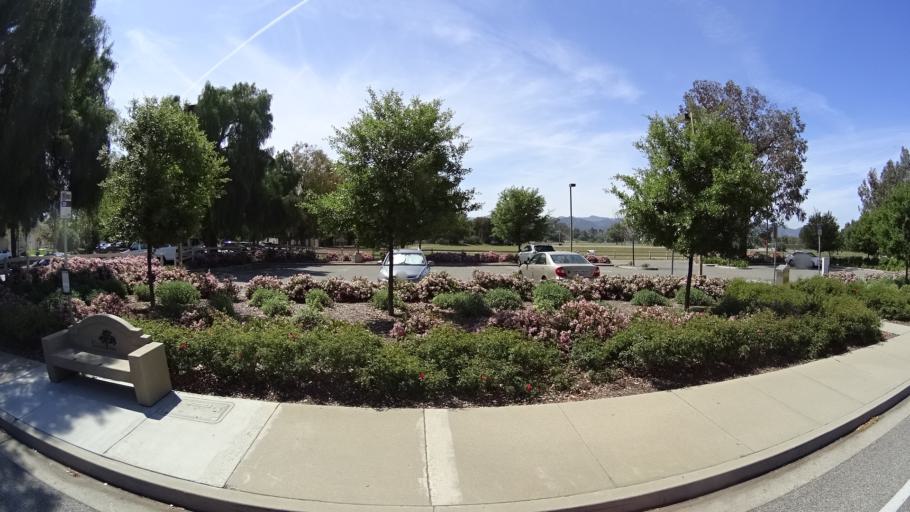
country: US
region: California
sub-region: Ventura County
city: Thousand Oaks
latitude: 34.1996
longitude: -118.8543
